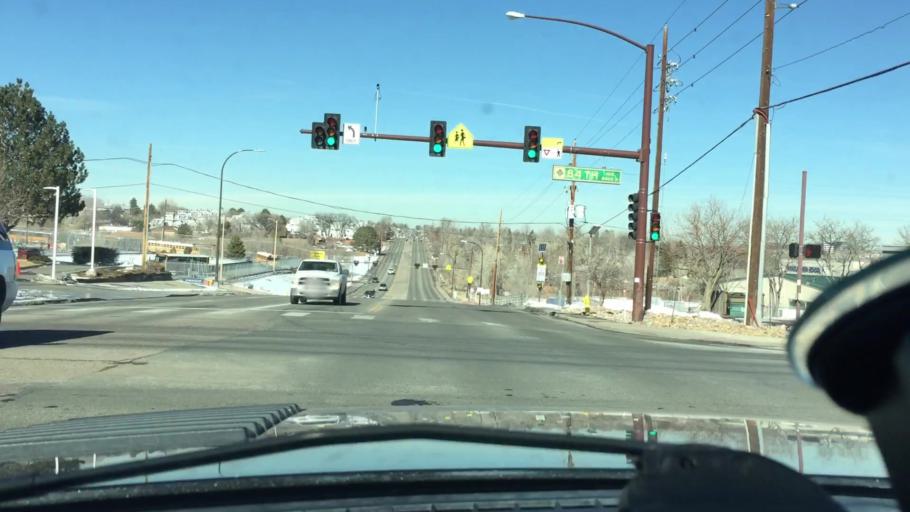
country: US
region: Colorado
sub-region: Adams County
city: Federal Heights
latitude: 39.8490
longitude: -104.9966
